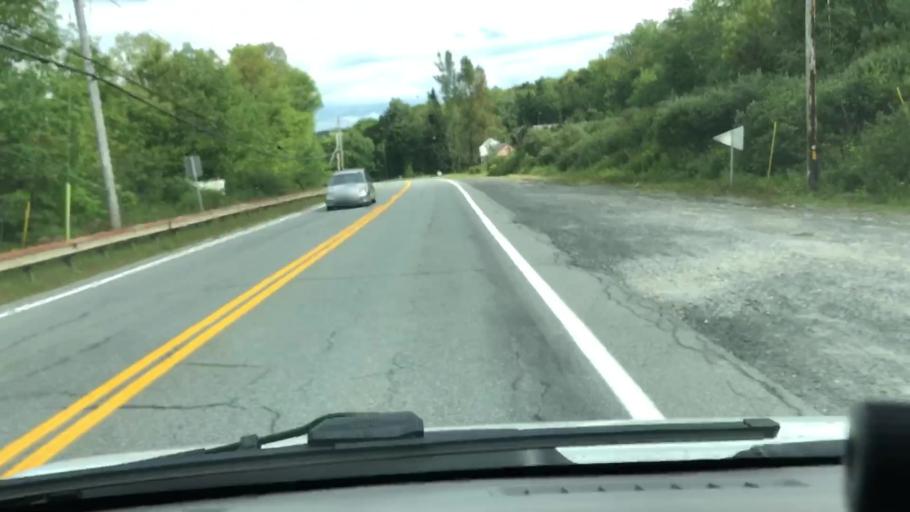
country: US
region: Massachusetts
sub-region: Berkshire County
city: North Adams
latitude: 42.6954
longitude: -73.0597
